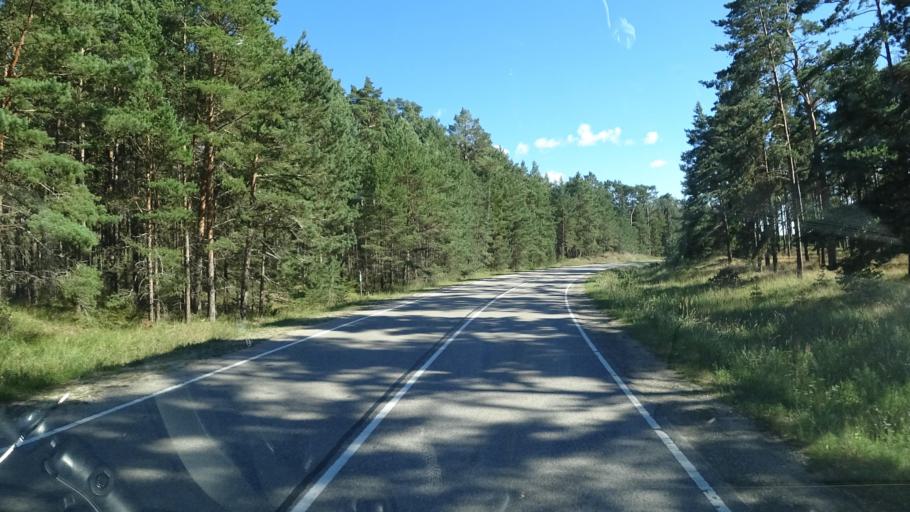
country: LV
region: Rojas
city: Roja
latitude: 57.7533
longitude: 22.5958
